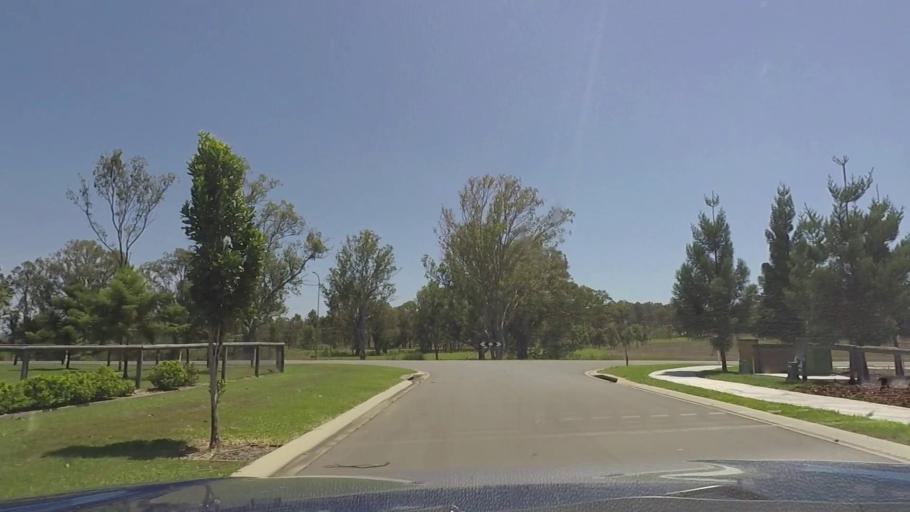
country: AU
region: Queensland
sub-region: Logan
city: Cedar Vale
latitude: -27.8863
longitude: 152.9829
